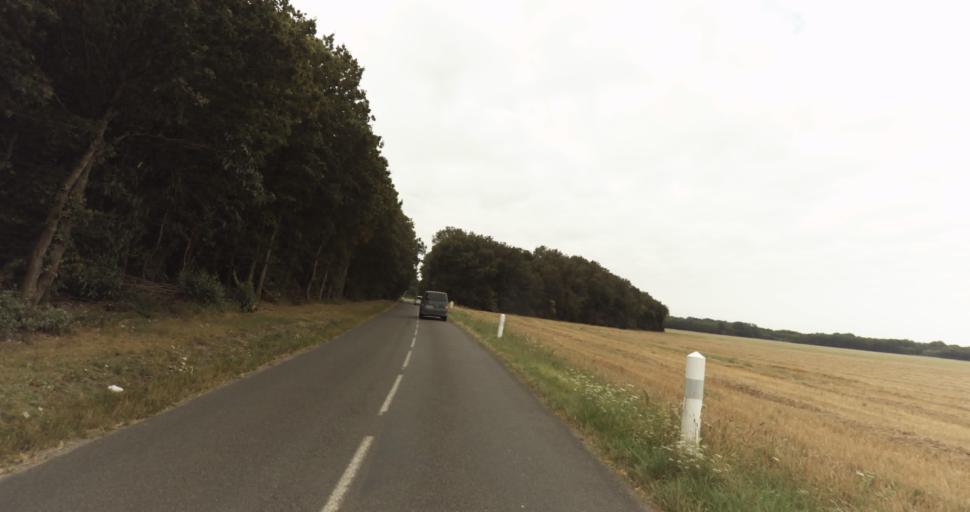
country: FR
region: Haute-Normandie
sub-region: Departement de l'Eure
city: Marcilly-sur-Eure
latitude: 48.8205
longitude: 1.3085
